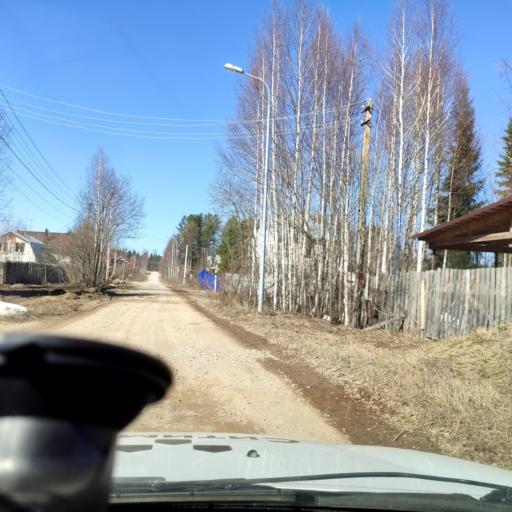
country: RU
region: Perm
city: Ferma
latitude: 57.9280
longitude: 56.4213
